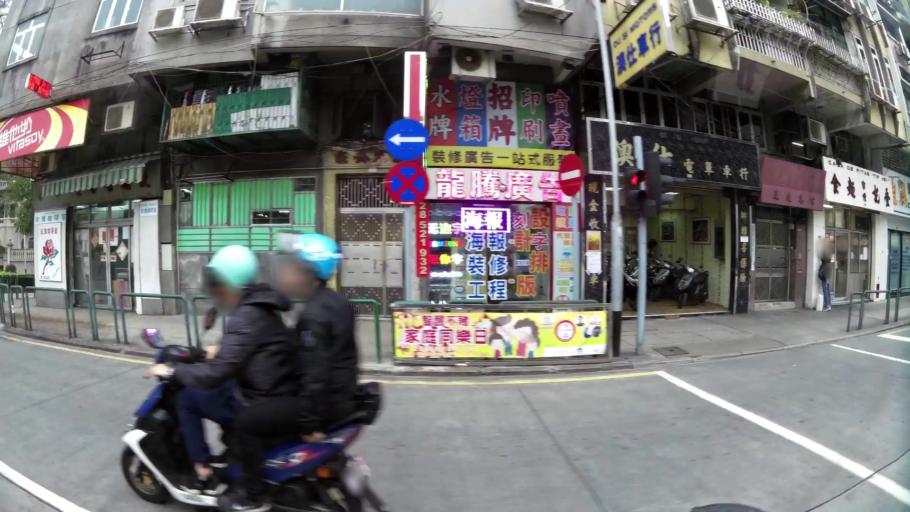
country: MO
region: Macau
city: Macau
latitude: 22.2000
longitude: 113.5496
